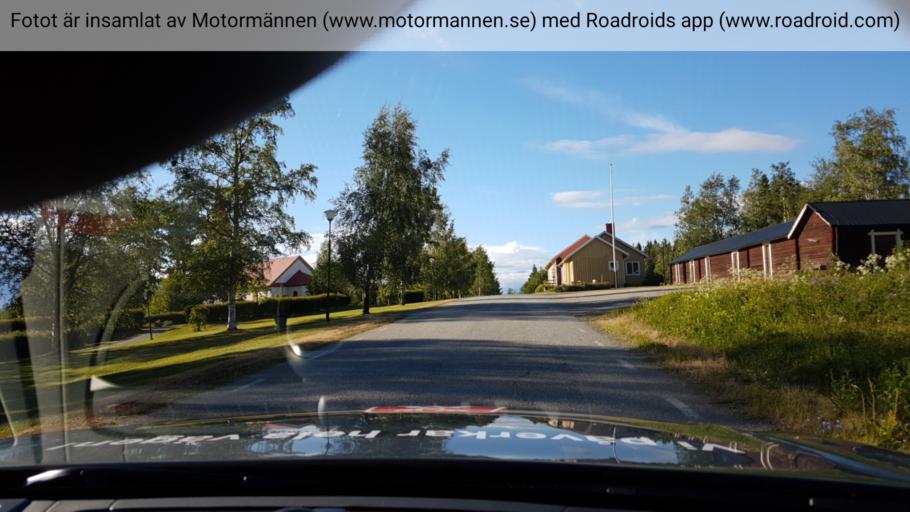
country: SE
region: Jaemtland
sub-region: Bergs Kommun
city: Hoverberg
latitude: 62.9164
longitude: 14.3796
